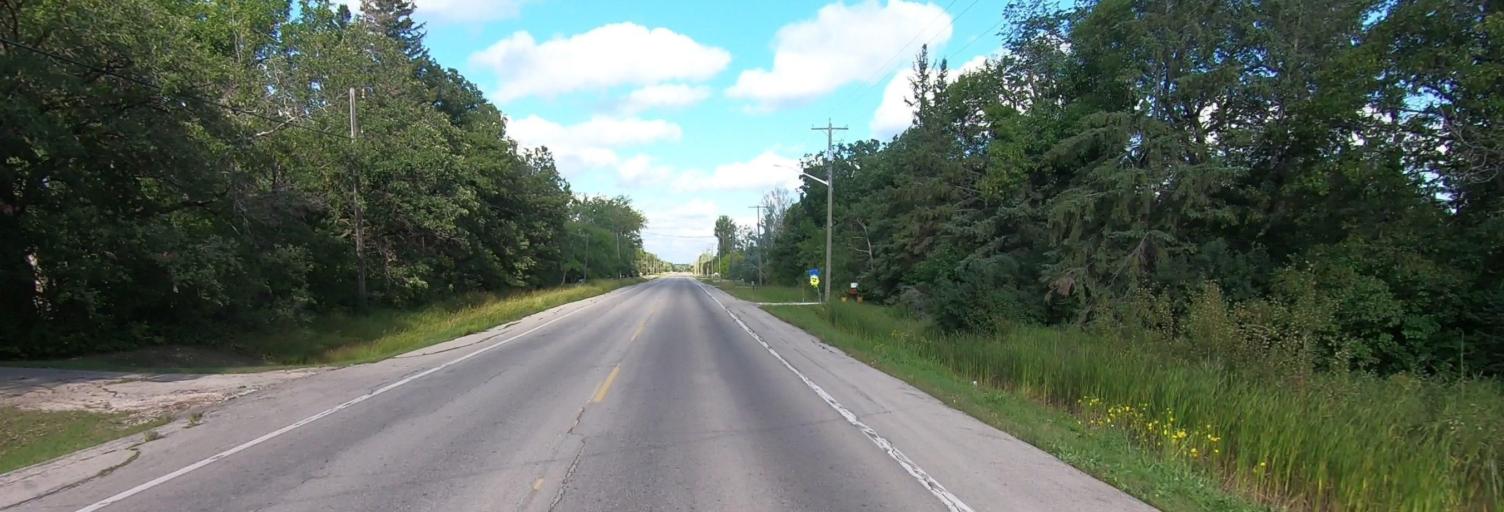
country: CA
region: Manitoba
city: Selkirk
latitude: 50.0268
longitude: -97.0224
